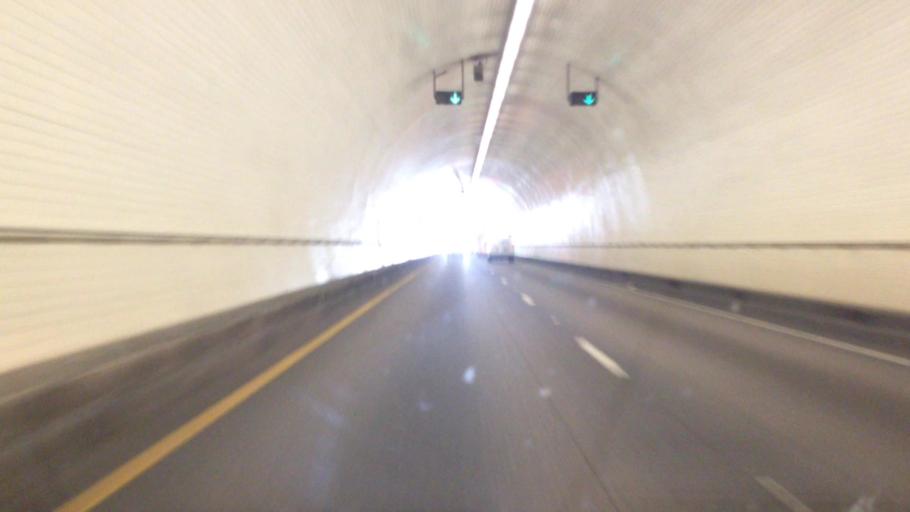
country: US
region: Alabama
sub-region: Mobile County
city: Mobile
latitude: 30.6906
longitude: -88.0337
